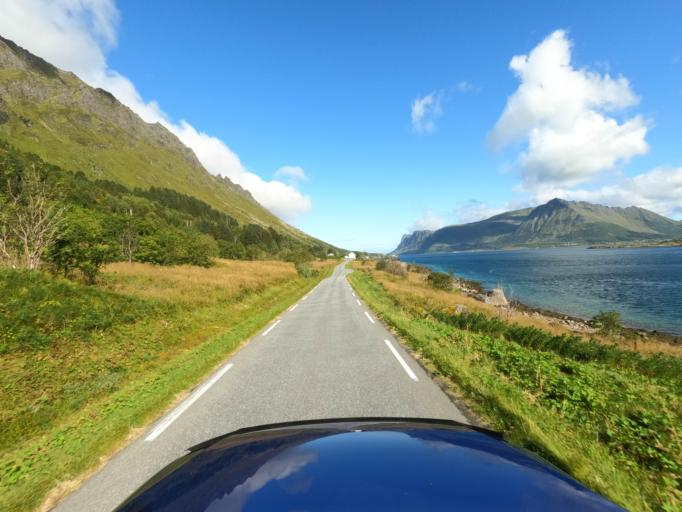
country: NO
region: Nordland
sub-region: Vagan
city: Kabelvag
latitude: 68.2667
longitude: 14.2476
